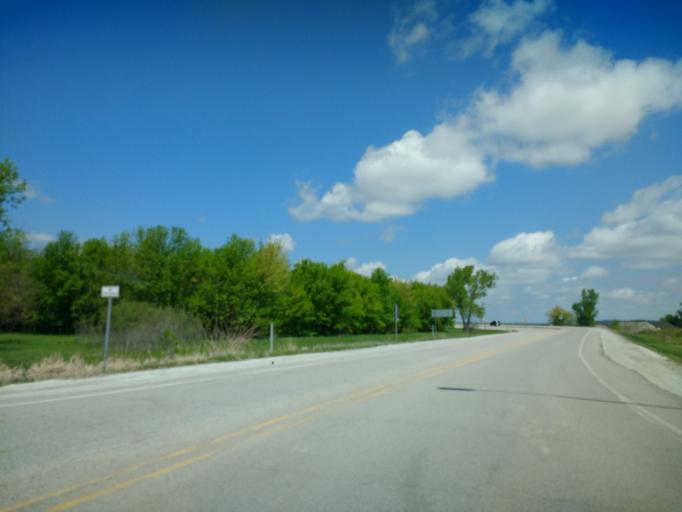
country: US
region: Iowa
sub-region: Harrison County
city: Missouri Valley
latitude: 41.4995
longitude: -95.8992
